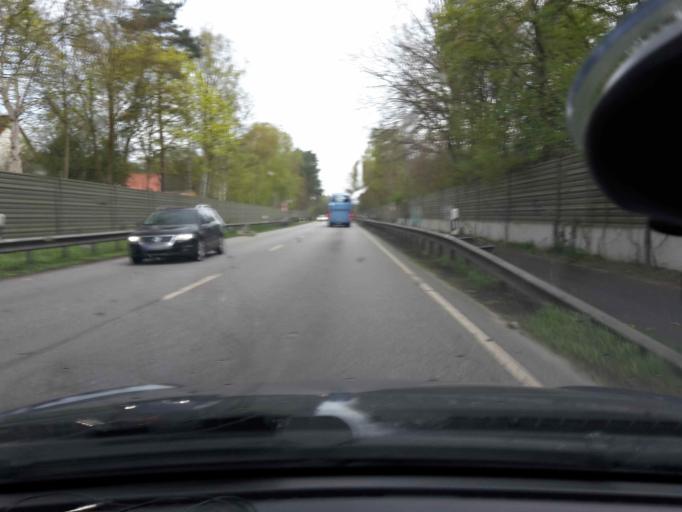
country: DE
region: Lower Saxony
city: Buxtehude
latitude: 53.4673
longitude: 9.6756
